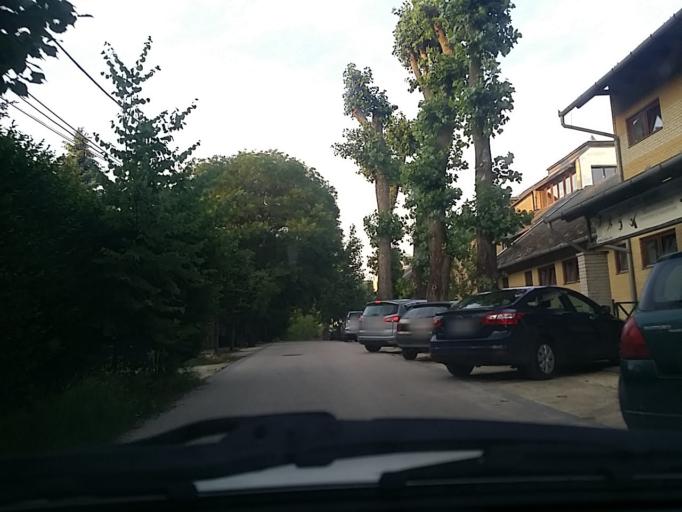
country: HU
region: Pest
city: Solymar
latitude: 47.5614
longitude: 18.9581
